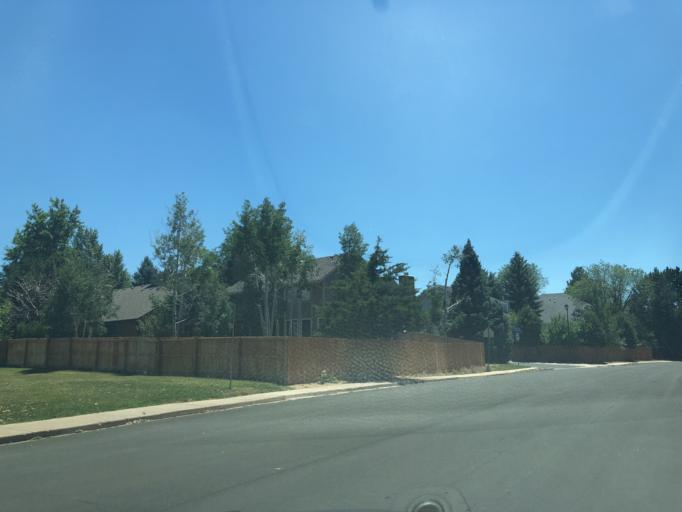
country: US
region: Colorado
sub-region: Arapahoe County
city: Dove Valley
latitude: 39.6183
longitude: -104.7809
